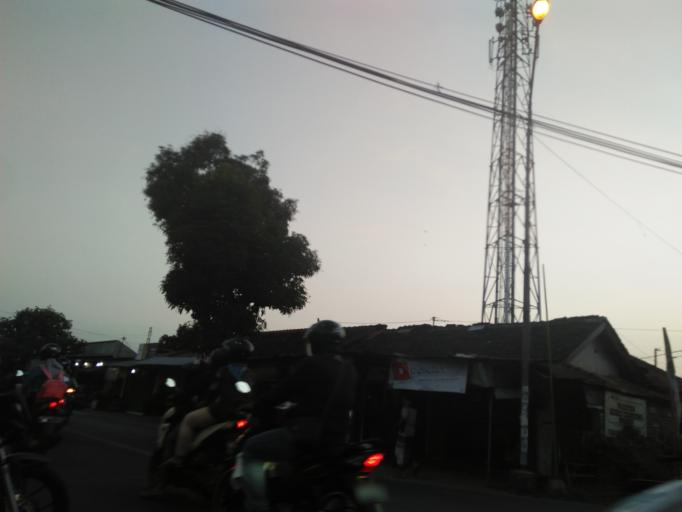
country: ID
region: Daerah Istimewa Yogyakarta
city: Sewon
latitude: -7.8434
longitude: 110.3913
